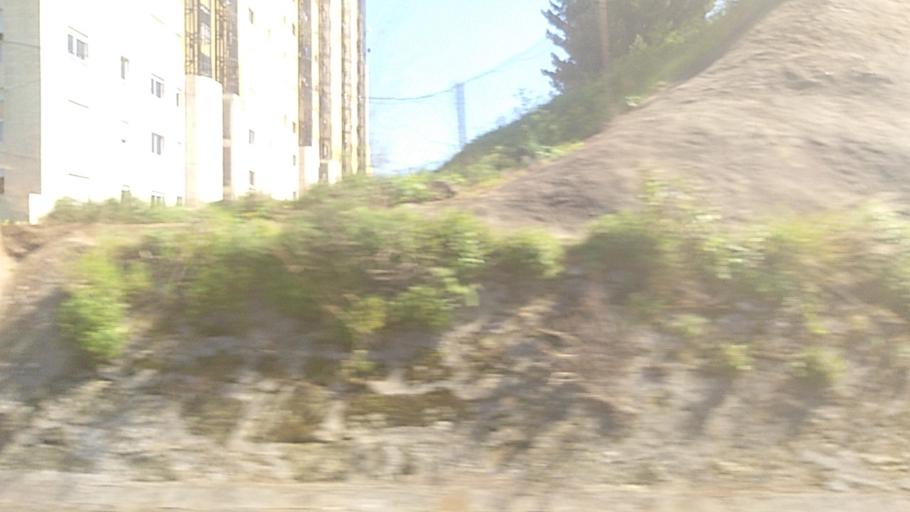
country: PT
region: Lisbon
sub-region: Lisbon
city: Lisbon
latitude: 38.7286
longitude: -9.1115
